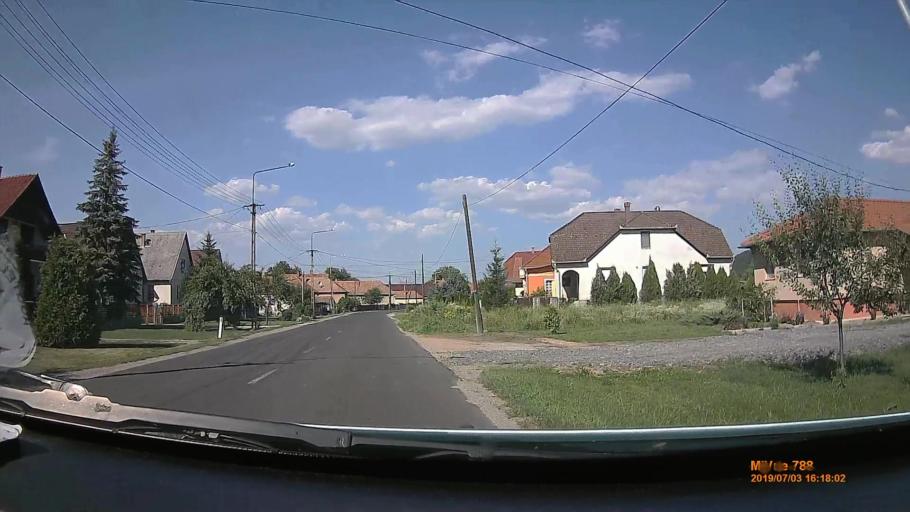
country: HU
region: Borsod-Abauj-Zemplen
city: Putnok
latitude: 48.2239
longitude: 20.4973
